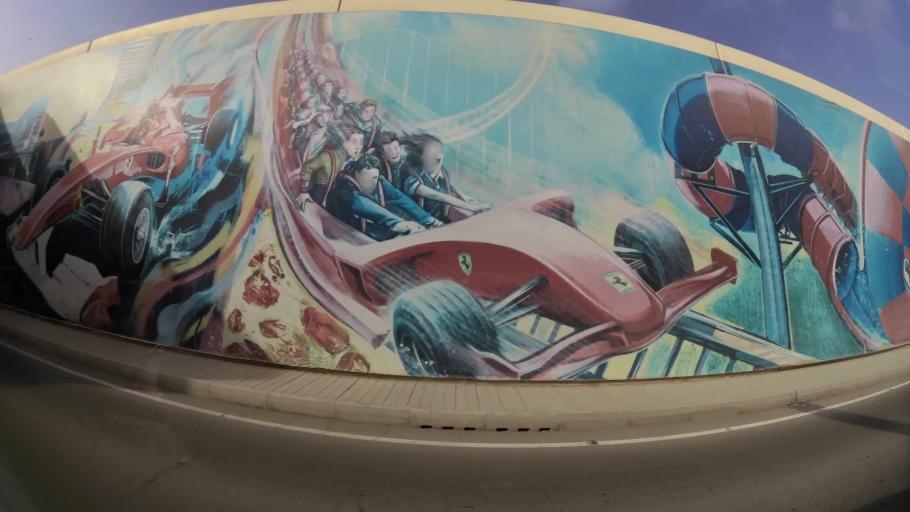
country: AE
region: Abu Dhabi
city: Abu Dhabi
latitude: 24.4611
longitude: 54.6147
